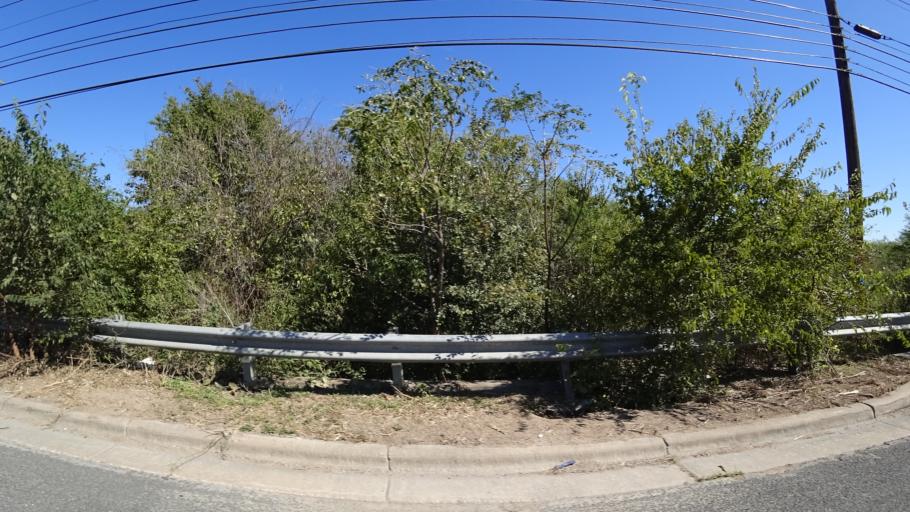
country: US
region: Texas
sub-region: Travis County
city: Austin
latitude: 30.1896
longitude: -97.6959
